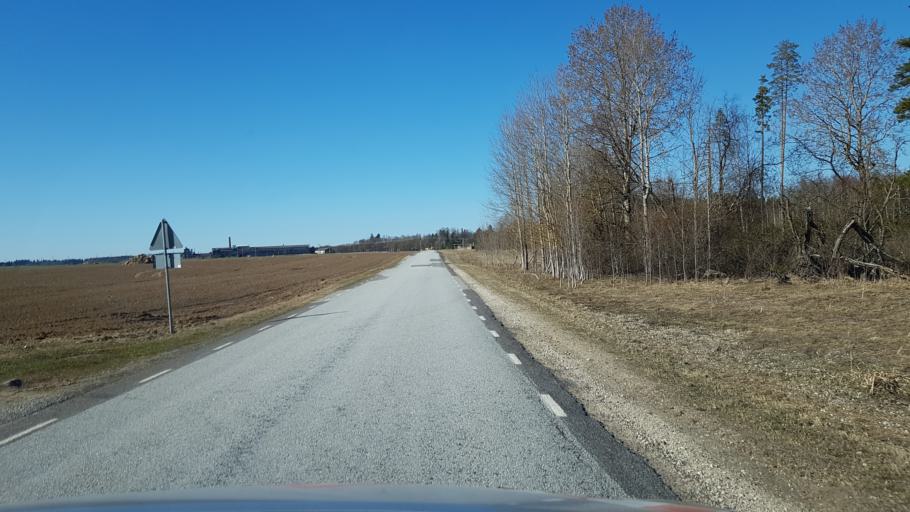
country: EE
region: Laeaene-Virumaa
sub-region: Viru-Nigula vald
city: Kunda
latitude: 59.3838
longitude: 26.5741
